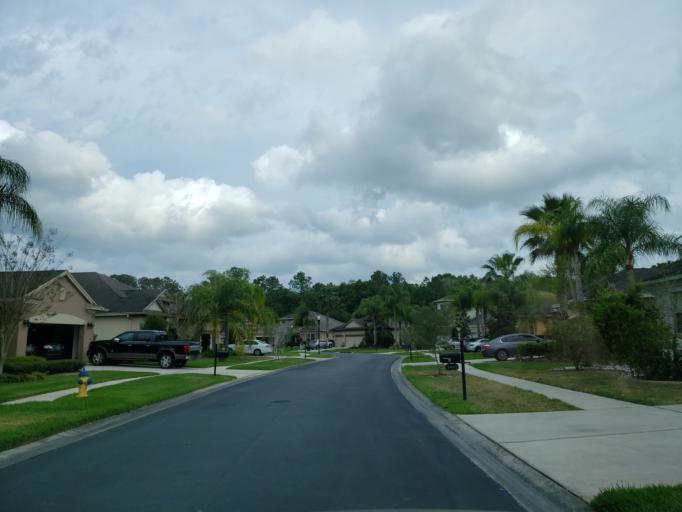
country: US
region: Florida
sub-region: Pasco County
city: Wesley Chapel
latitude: 28.2070
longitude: -82.3612
